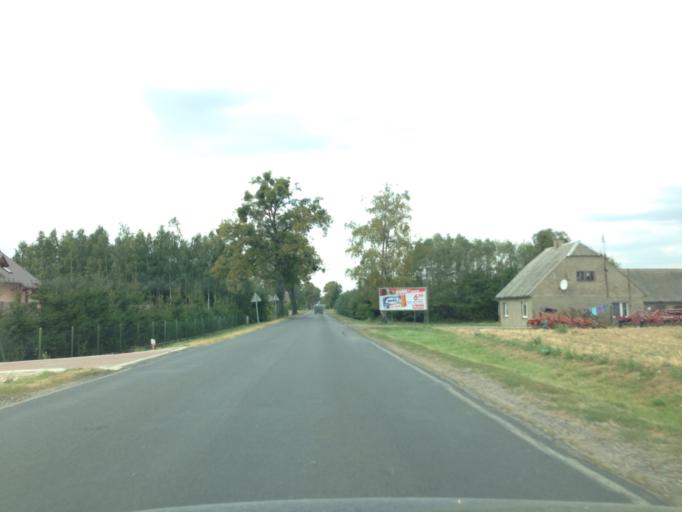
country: PL
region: Kujawsko-Pomorskie
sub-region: Powiat golubsko-dobrzynski
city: Golub-Dobrzyn
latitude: 53.1365
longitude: 19.0051
